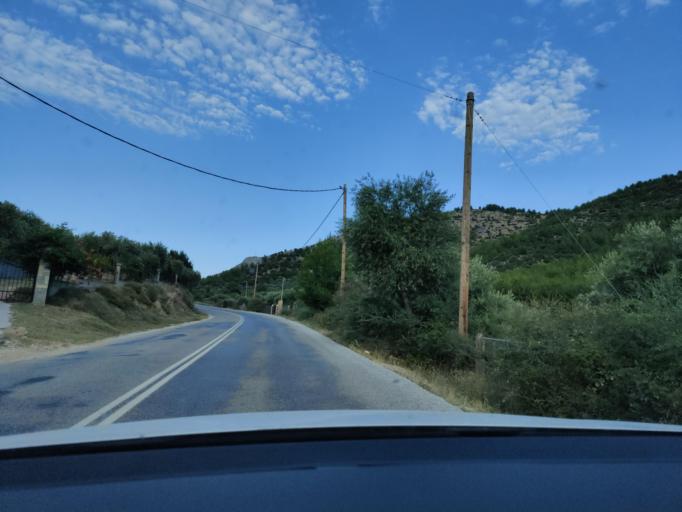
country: GR
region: East Macedonia and Thrace
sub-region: Nomos Kavalas
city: Limenaria
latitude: 40.6133
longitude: 24.6333
